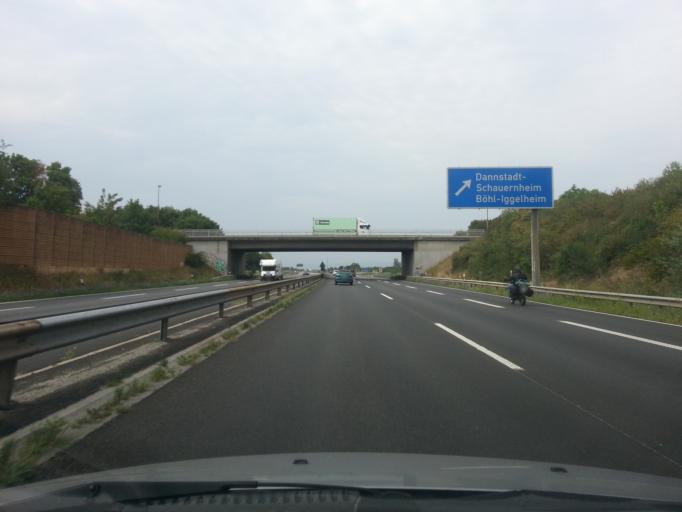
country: DE
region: Rheinland-Pfalz
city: Dannstadt-Schauernheim
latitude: 49.4351
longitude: 8.3080
